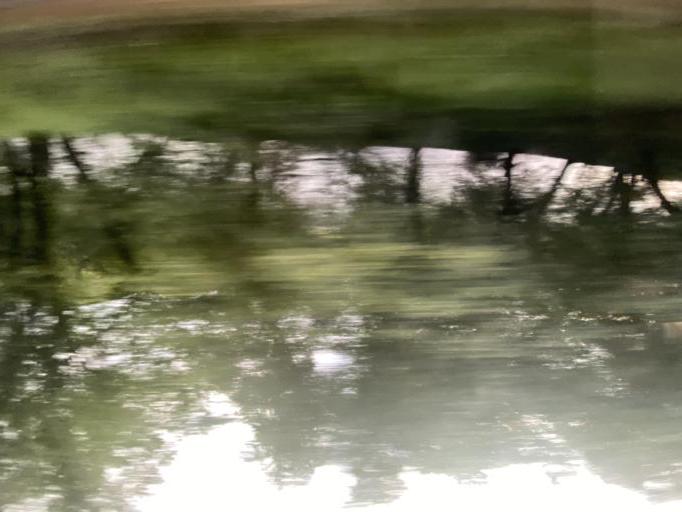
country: US
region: West Virginia
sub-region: Mineral County
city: Fort Ashby
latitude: 39.5214
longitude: -78.5427
